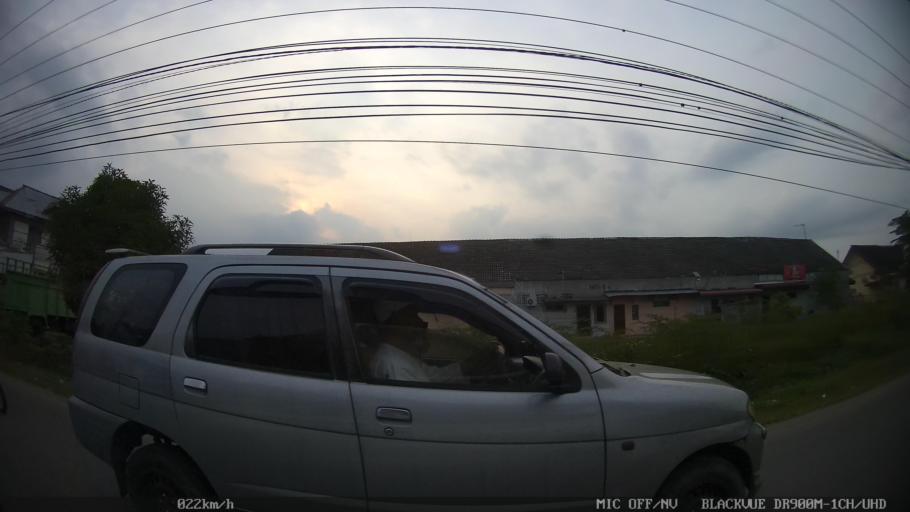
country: ID
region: North Sumatra
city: Sunggal
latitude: 3.5855
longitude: 98.5992
